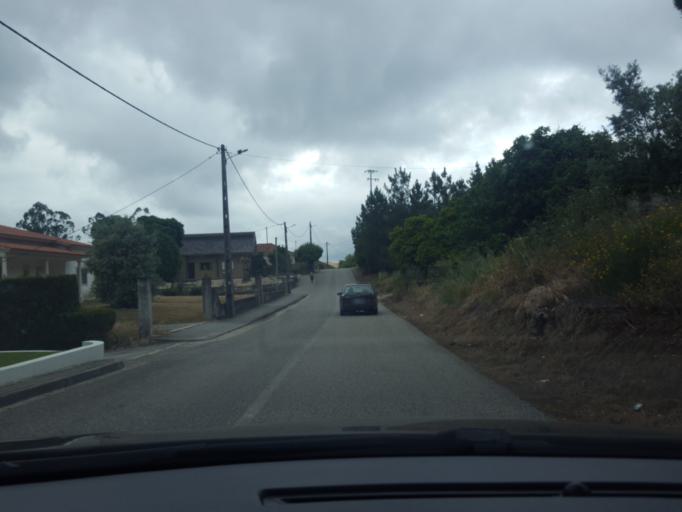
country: PT
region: Leiria
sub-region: Leiria
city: Caranguejeira
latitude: 39.7925
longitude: -8.7508
